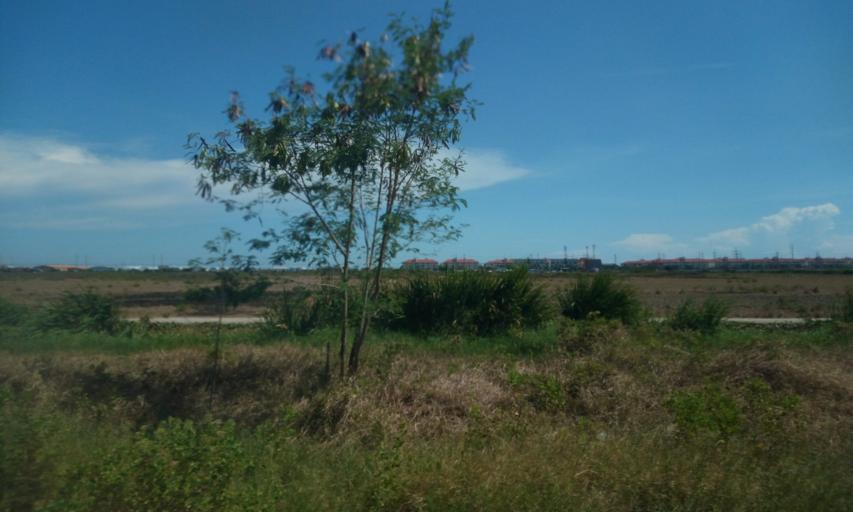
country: TH
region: Samut Prakan
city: Bang Bo District
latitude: 13.5606
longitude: 100.7767
